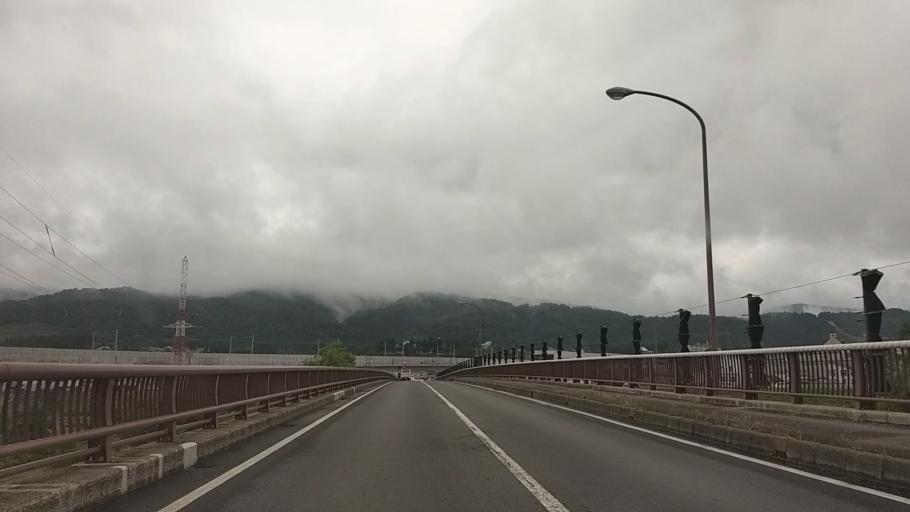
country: JP
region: Nagano
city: Iiyama
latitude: 36.8412
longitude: 138.3652
